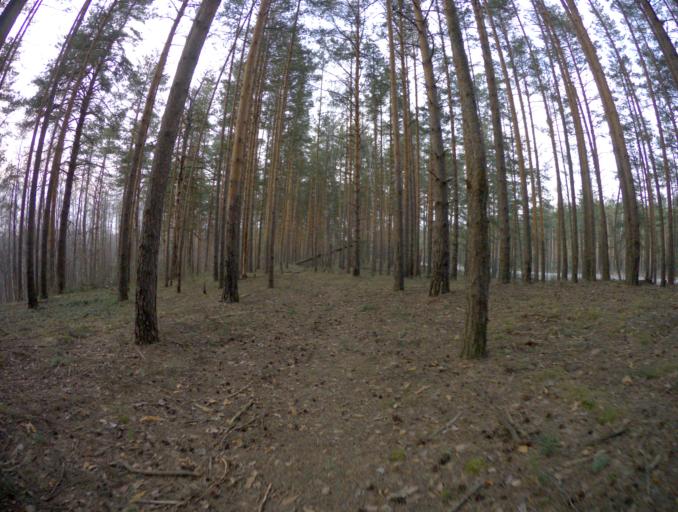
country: RU
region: Vladimir
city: Kommunar
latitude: 56.0707
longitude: 40.4318
